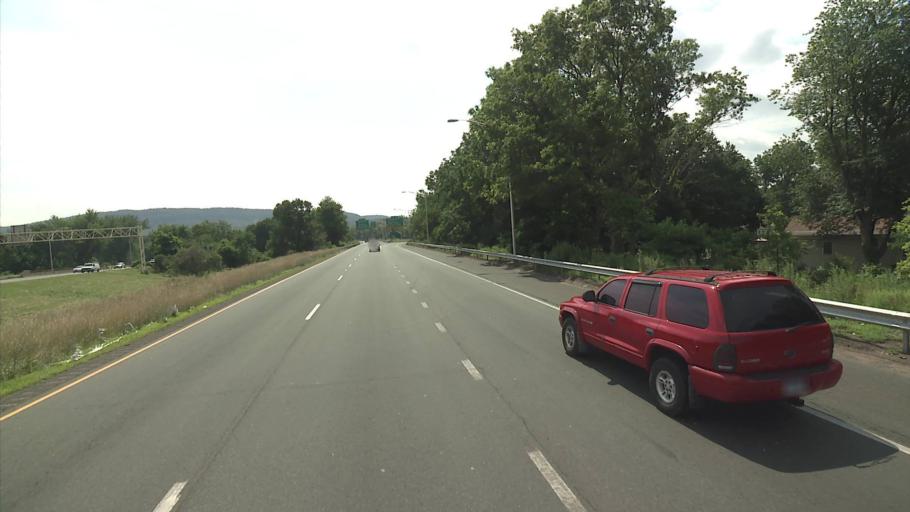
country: US
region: Connecticut
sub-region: New Haven County
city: Meriden
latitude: 41.5402
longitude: -72.7733
